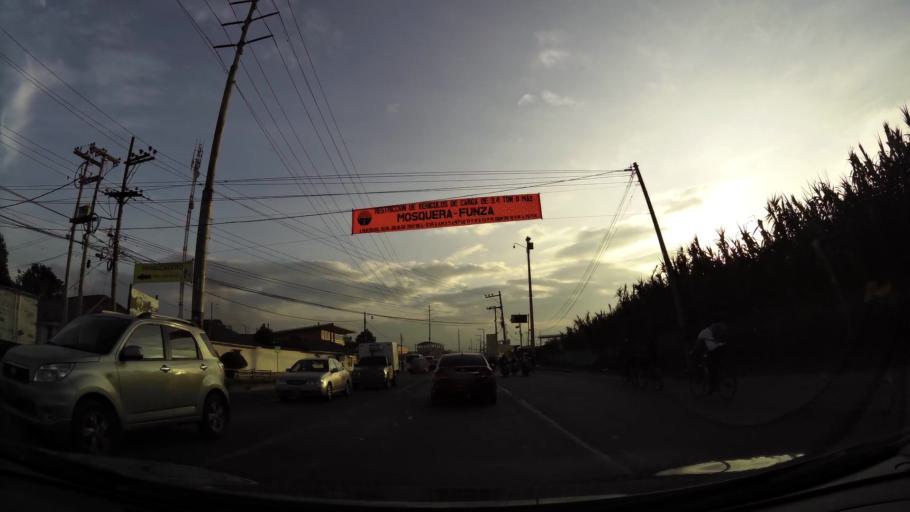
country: CO
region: Cundinamarca
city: Funza
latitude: 4.7206
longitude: -74.1980
